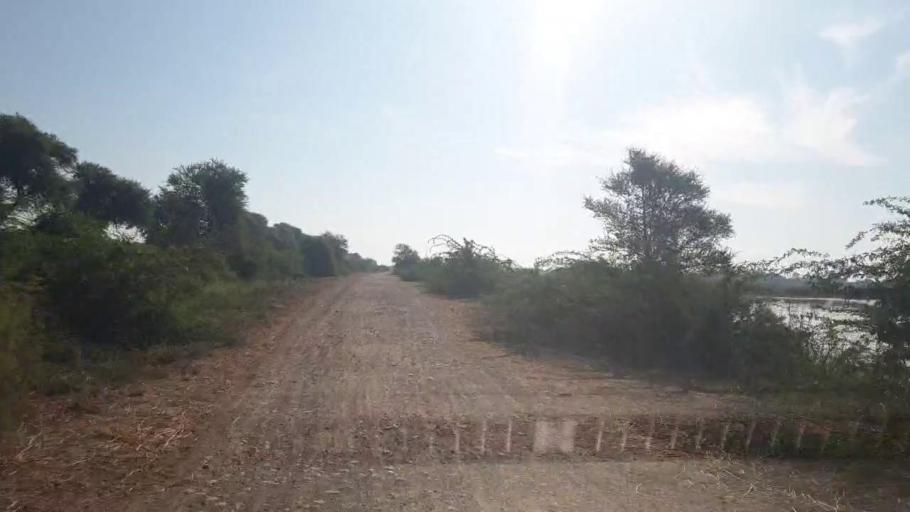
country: PK
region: Sindh
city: Rajo Khanani
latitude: 24.9759
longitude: 68.7811
